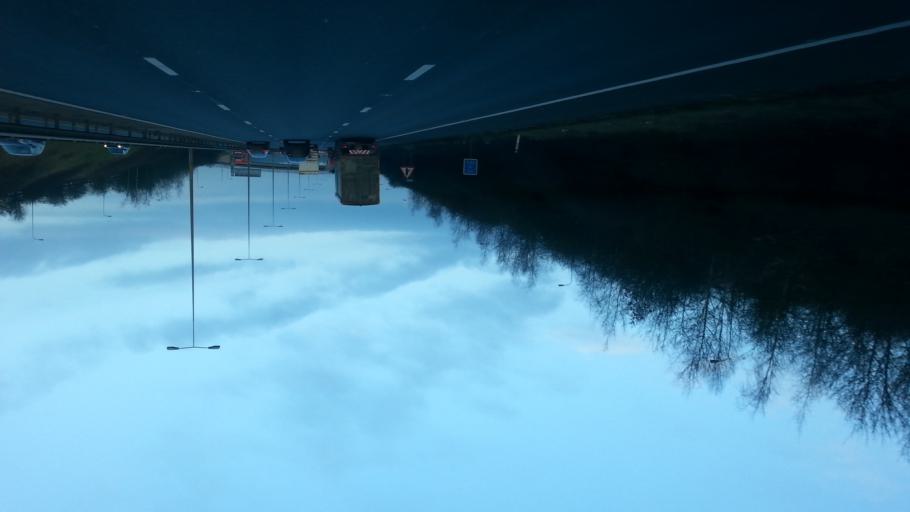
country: GB
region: England
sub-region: Worcestershire
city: Worcester
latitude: 52.1695
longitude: -2.1797
